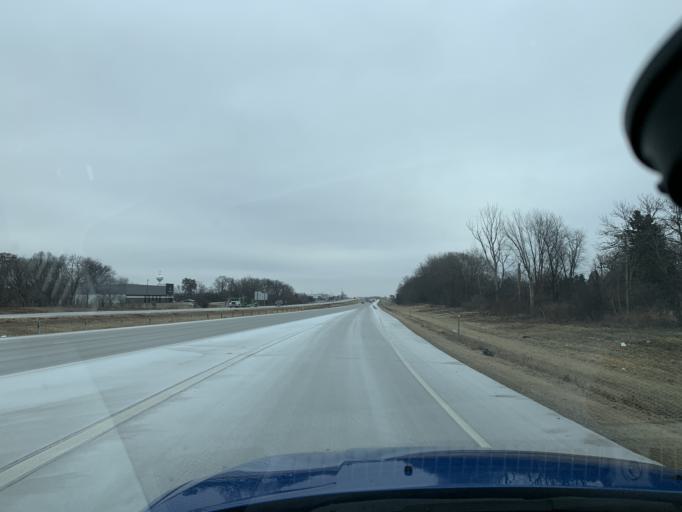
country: US
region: Wisconsin
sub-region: Dane County
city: Sun Prairie
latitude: 43.1979
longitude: -89.2074
